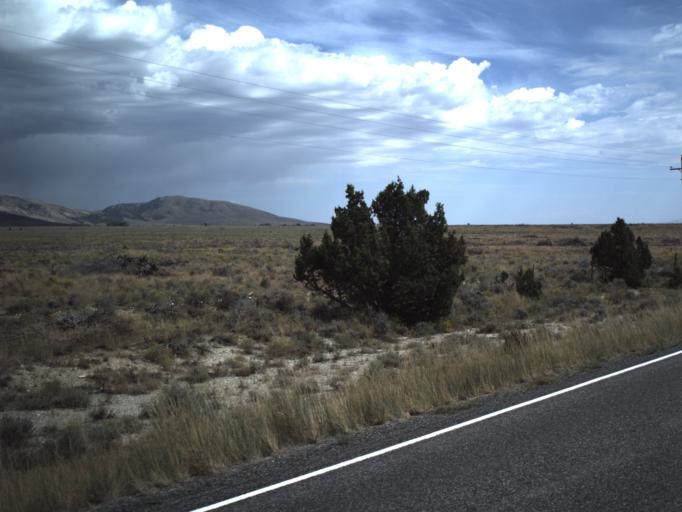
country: US
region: Idaho
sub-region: Cassia County
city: Burley
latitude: 41.8174
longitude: -113.3938
